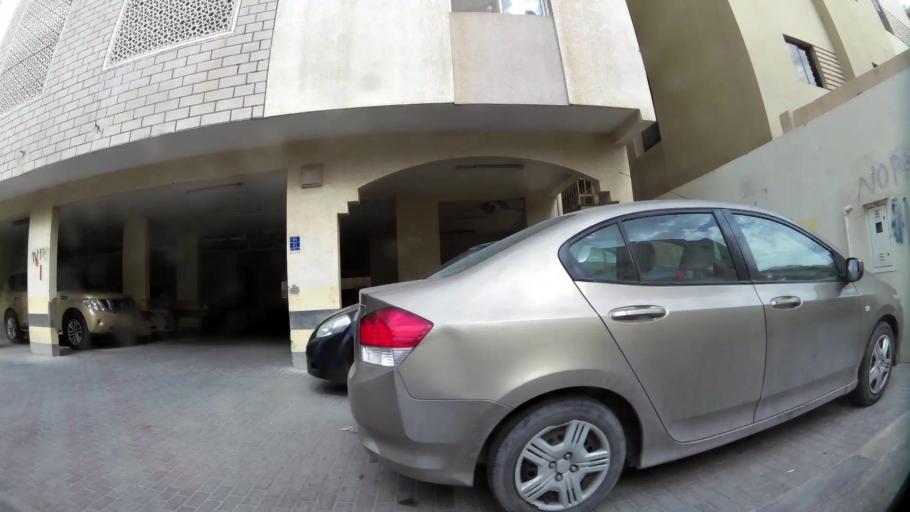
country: QA
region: Baladiyat ad Dawhah
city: Doha
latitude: 25.2872
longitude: 51.5153
